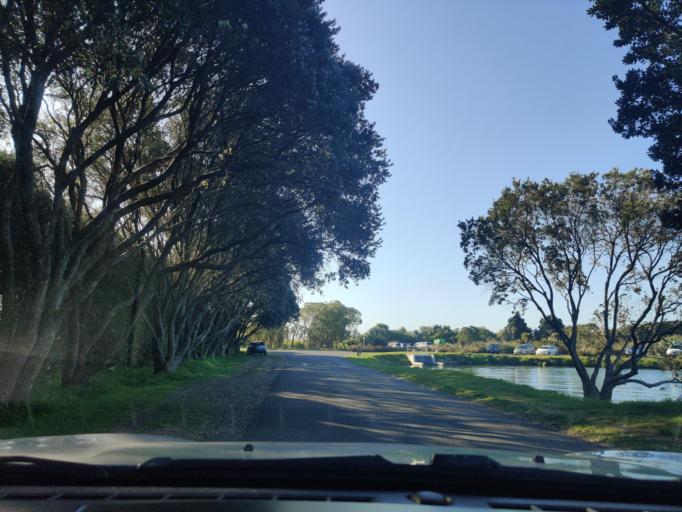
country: NZ
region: Taranaki
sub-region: New Plymouth District
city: New Plymouth
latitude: -39.0393
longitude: 174.1138
